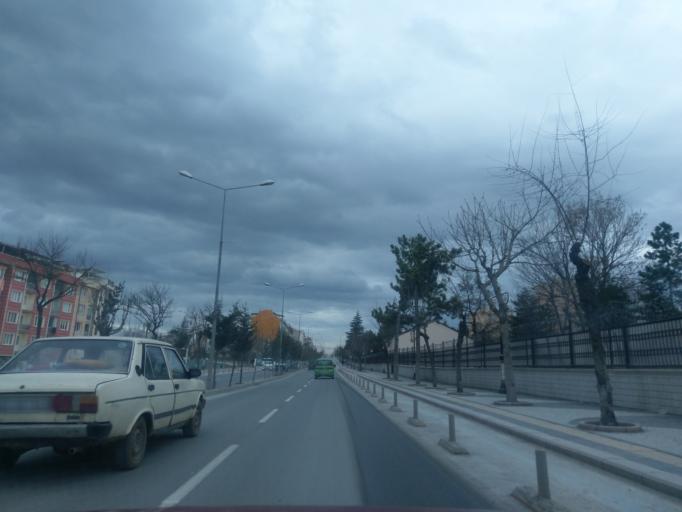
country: TR
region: Kuetahya
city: Kutahya
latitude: 39.4103
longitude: 30.0030
